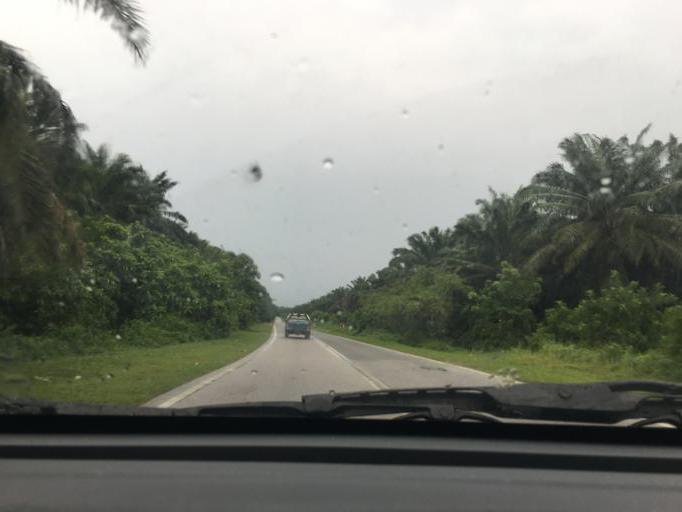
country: MY
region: Kedah
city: Sungai Petani
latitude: 5.6381
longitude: 100.6285
